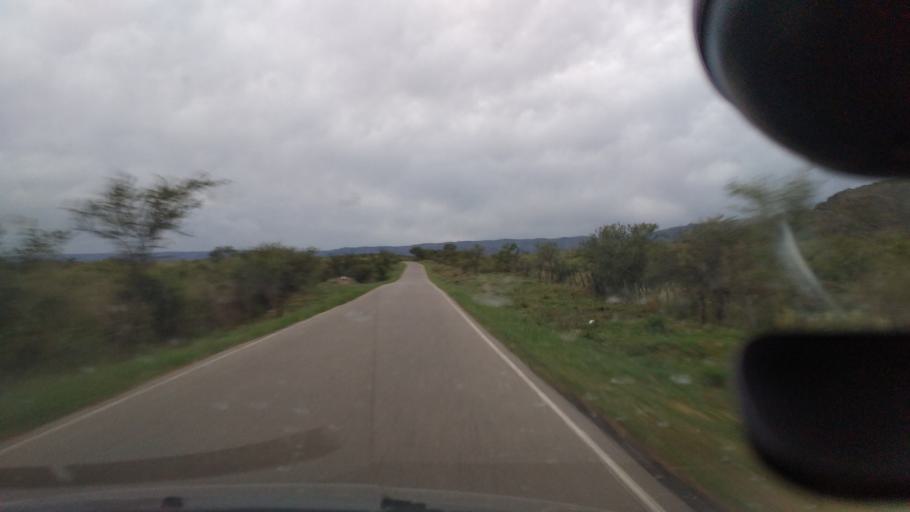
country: AR
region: Cordoba
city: Villa Las Rosas
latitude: -31.8859
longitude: -65.0268
